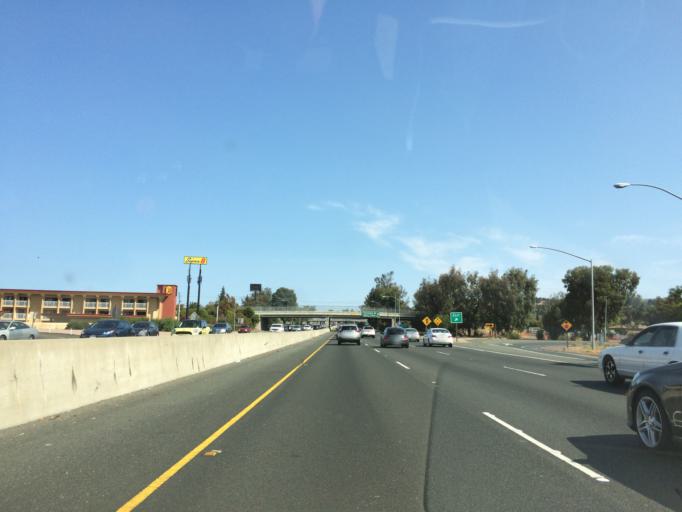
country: US
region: California
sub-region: Solano County
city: Vallejo
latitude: 38.1038
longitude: -122.2297
